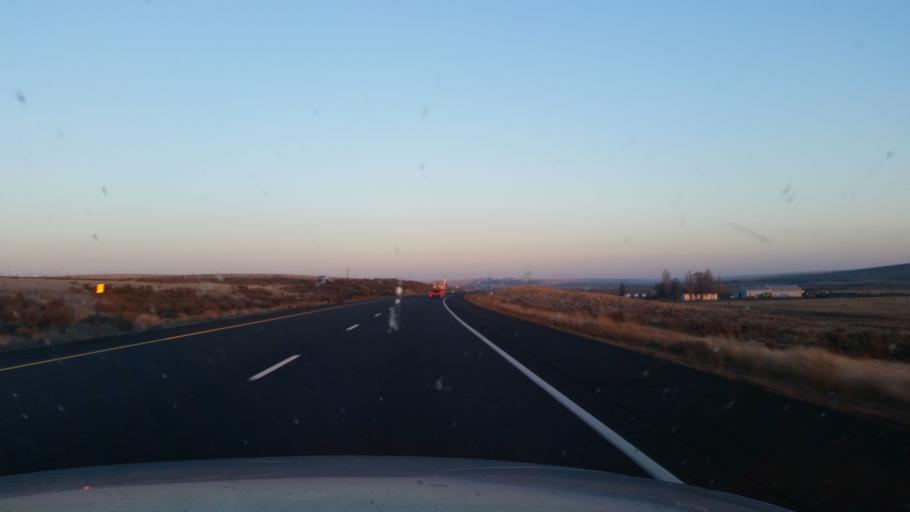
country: US
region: Washington
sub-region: Grant County
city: Warden
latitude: 47.0874
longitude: -118.9263
